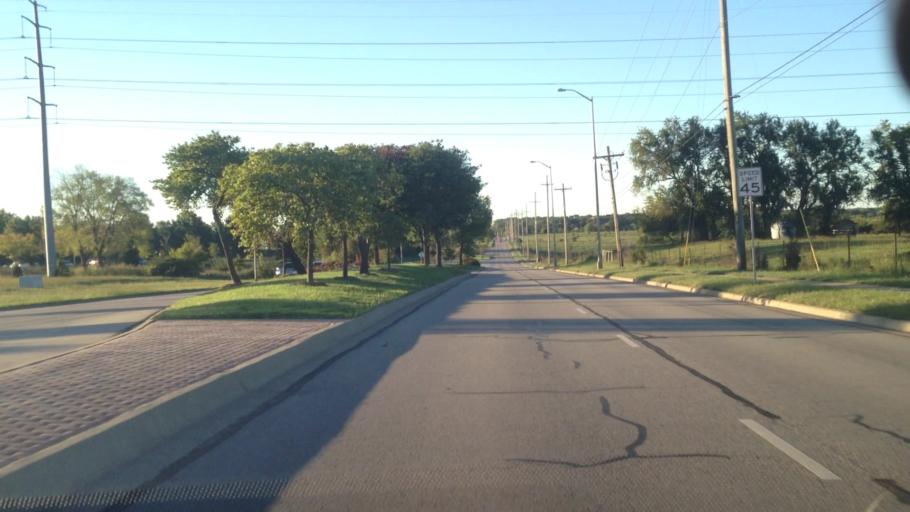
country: US
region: Kansas
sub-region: Johnson County
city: Olathe
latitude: 38.9356
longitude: -94.7976
